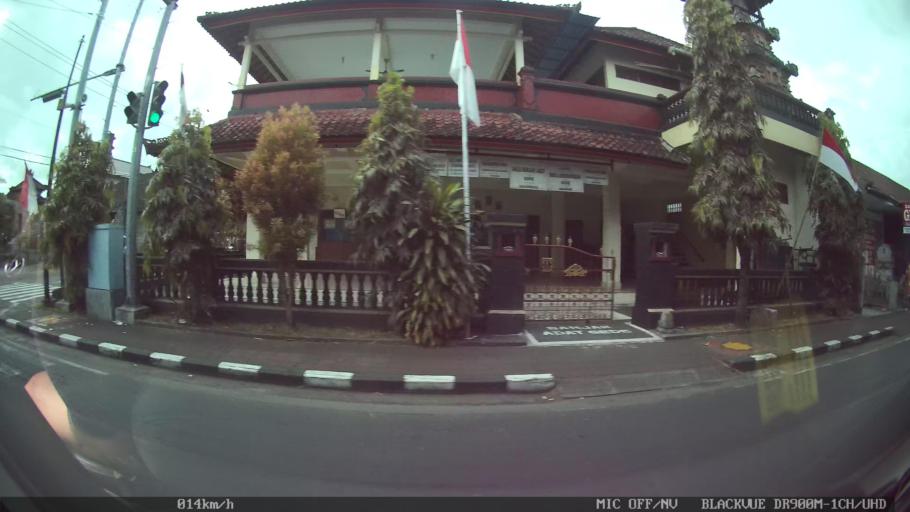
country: ID
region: Bali
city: Banjar Pekenjelodan
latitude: -8.5930
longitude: 115.1755
